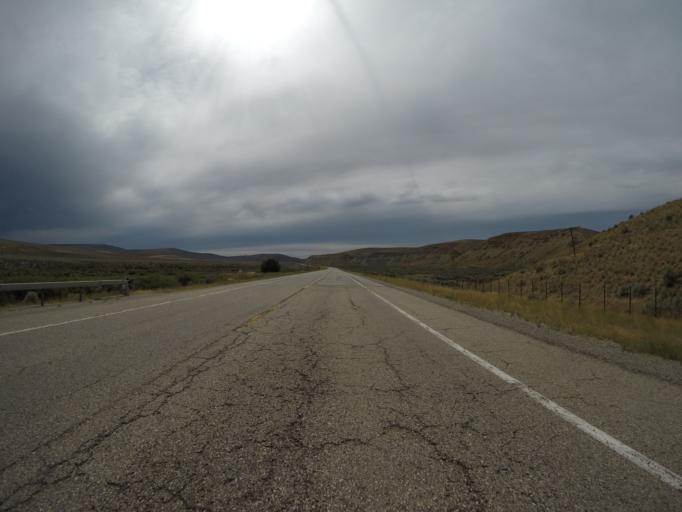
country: US
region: Wyoming
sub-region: Lincoln County
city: Kemmerer
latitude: 41.8230
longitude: -110.8708
